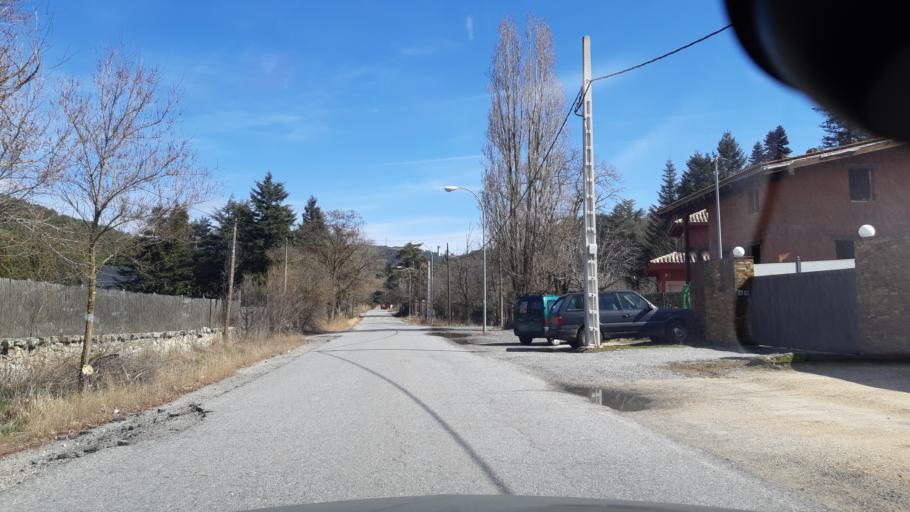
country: ES
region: Madrid
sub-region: Provincia de Madrid
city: Guadarrama
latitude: 40.7125
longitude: -4.1805
